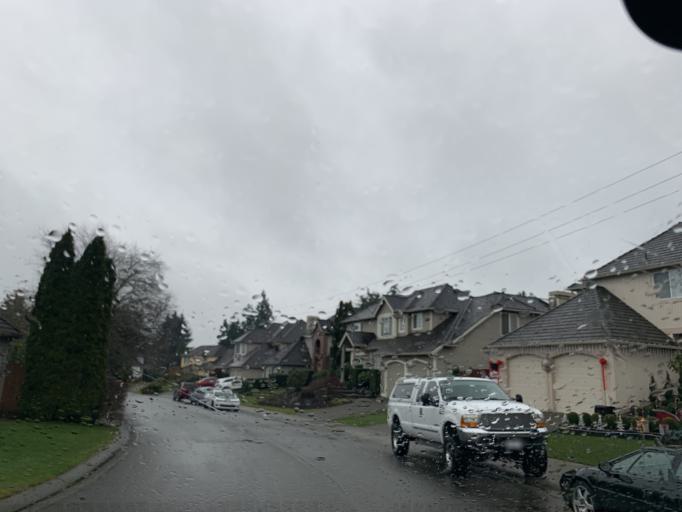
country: US
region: Washington
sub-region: King County
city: Kingsgate
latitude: 47.7333
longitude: -122.1630
